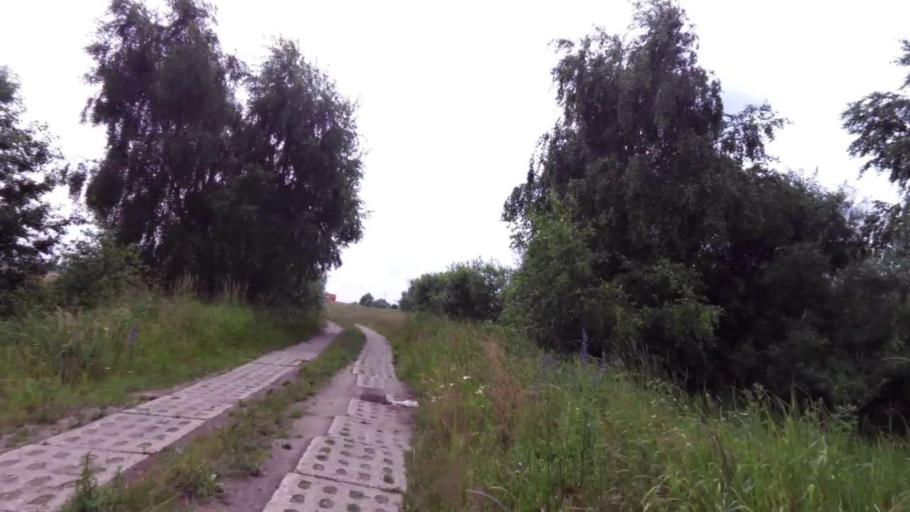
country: PL
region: West Pomeranian Voivodeship
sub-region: Powiat policki
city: Police
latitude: 53.4882
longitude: 14.6978
